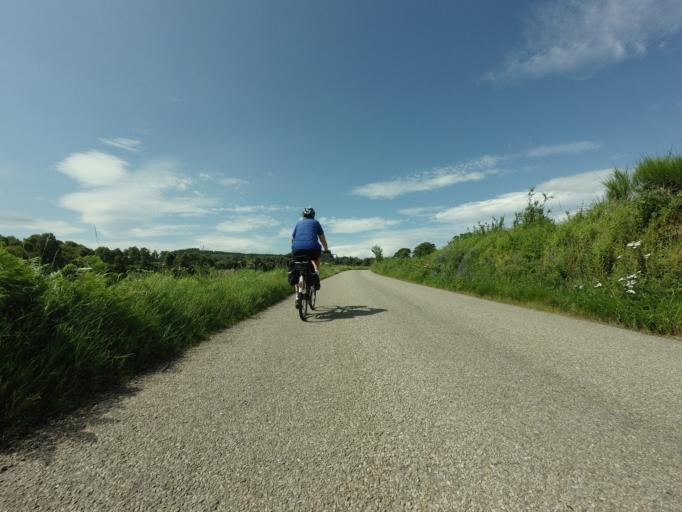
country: GB
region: Scotland
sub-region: Highland
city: Inverness
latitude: 57.5225
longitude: -4.3080
